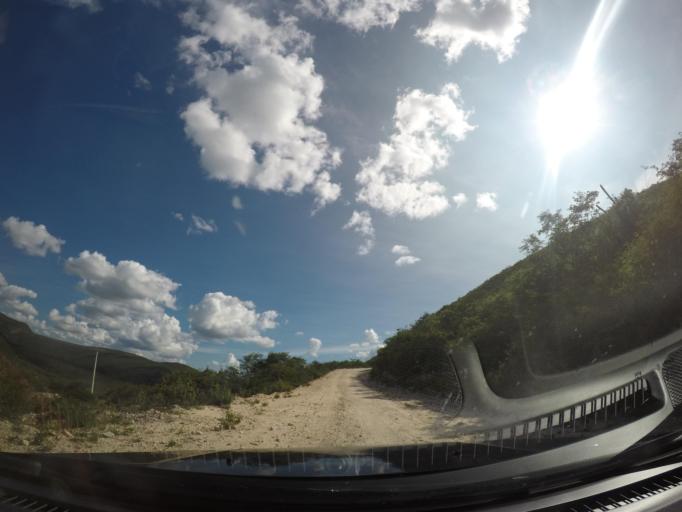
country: BR
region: Bahia
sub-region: Barra Da Estiva
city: Barra da Estiva
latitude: -13.2109
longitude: -41.5911
